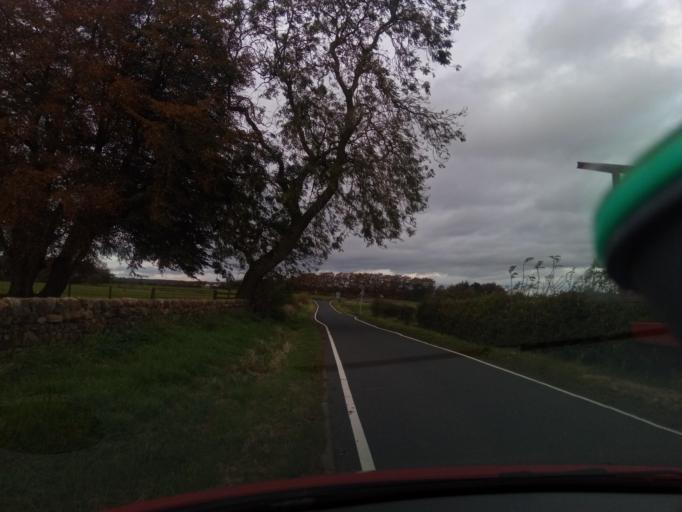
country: GB
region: Scotland
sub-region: West Lothian
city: Blackburn
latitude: 55.8312
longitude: -3.6092
